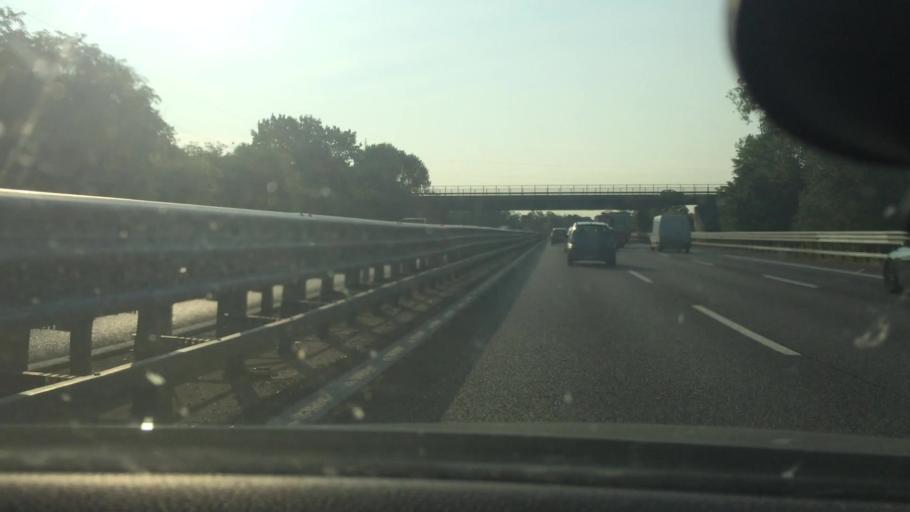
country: IT
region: Lombardy
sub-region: Citta metropolitana di Milano
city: Buccinasco
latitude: 45.4131
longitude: 9.0999
